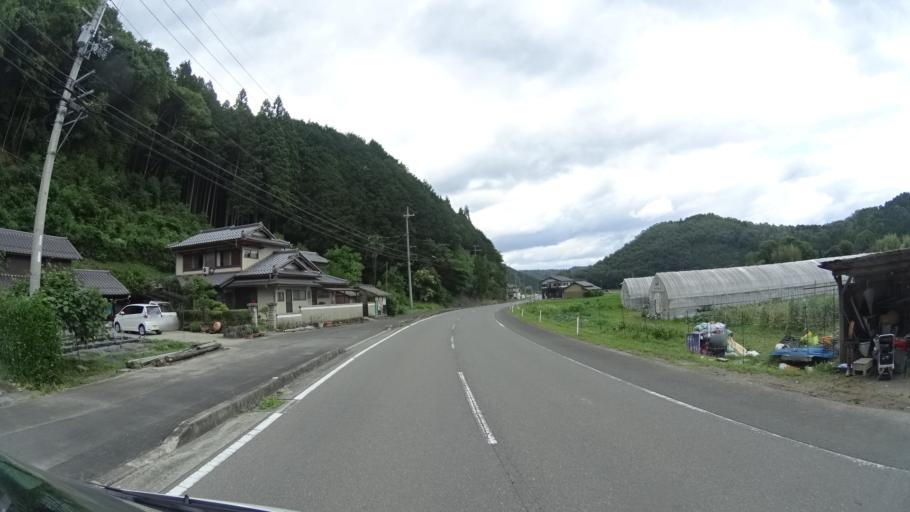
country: JP
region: Kyoto
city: Kameoka
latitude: 35.0991
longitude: 135.4330
